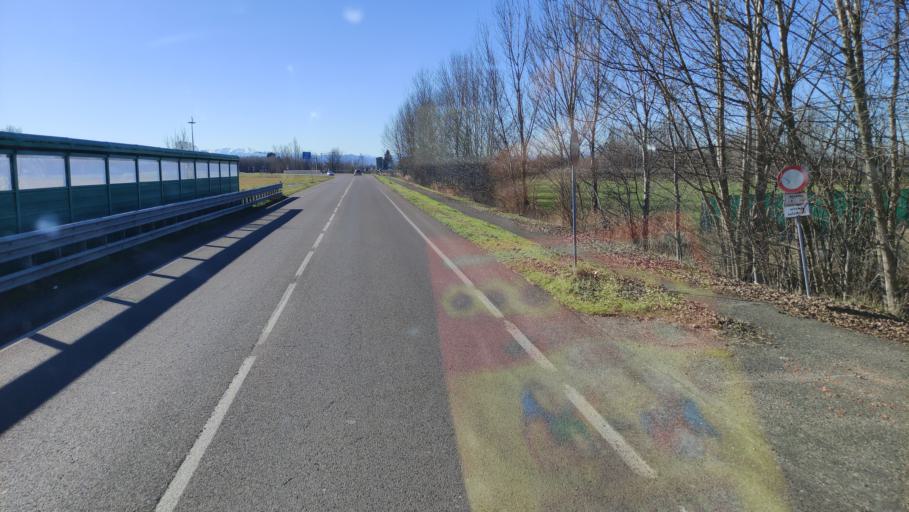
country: IT
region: Emilia-Romagna
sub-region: Provincia di Reggio Emilia
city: San Martino in Rio
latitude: 44.7367
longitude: 10.7688
